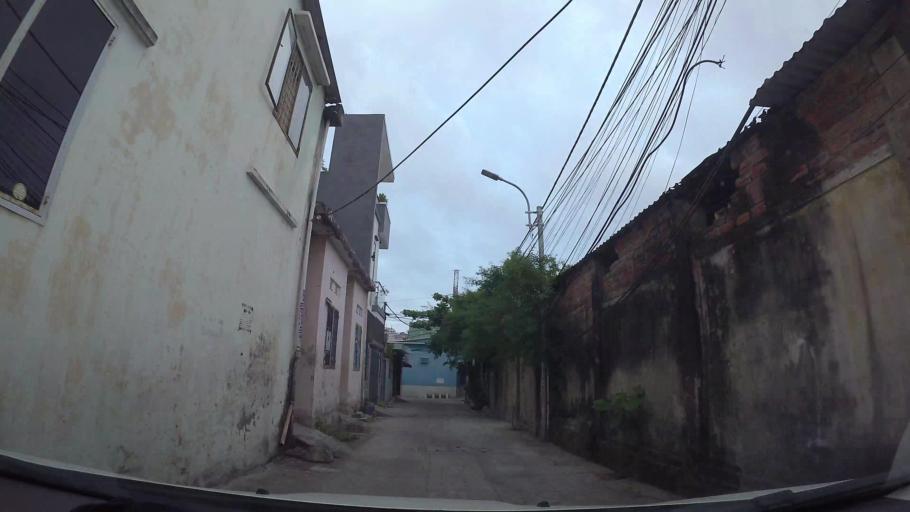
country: VN
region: Da Nang
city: Son Tra
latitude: 16.0610
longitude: 108.2375
